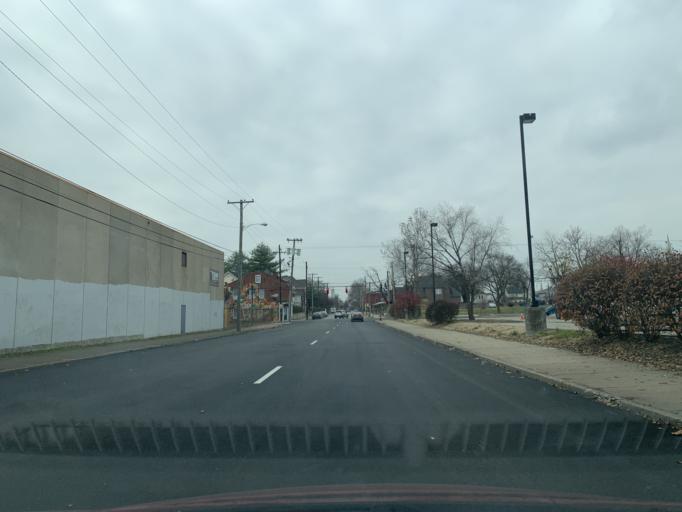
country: US
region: Kentucky
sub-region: Jefferson County
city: Louisville
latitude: 38.2530
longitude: -85.7746
